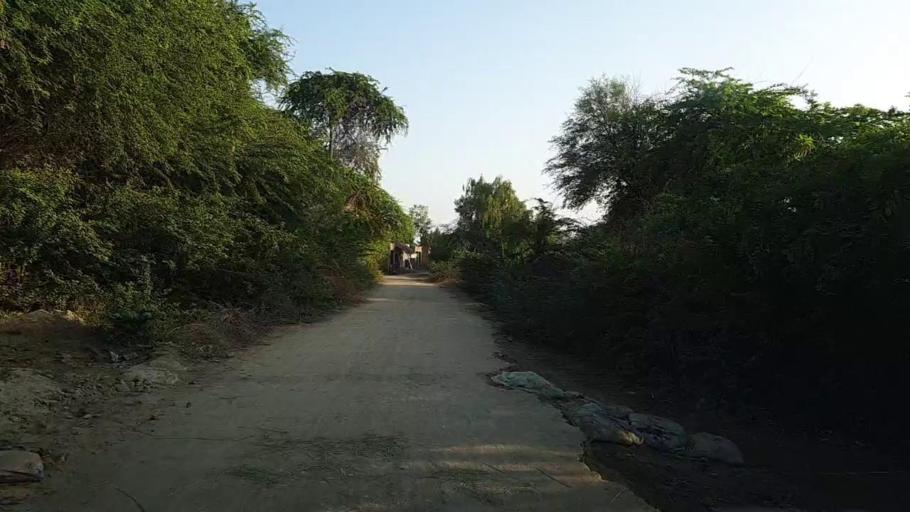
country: PK
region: Sindh
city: Kario
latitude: 24.6896
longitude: 68.6731
